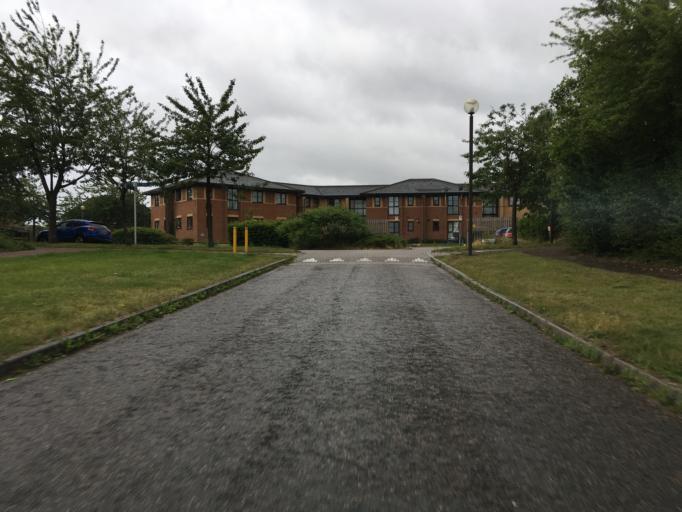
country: GB
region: England
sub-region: Milton Keynes
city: Simpson
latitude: 52.0328
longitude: -0.6960
